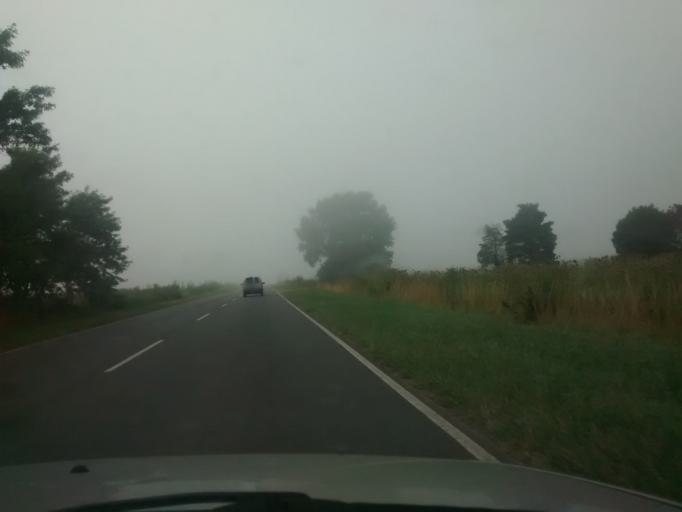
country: AR
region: Buenos Aires
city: Ranchos
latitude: -35.3595
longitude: -58.2496
